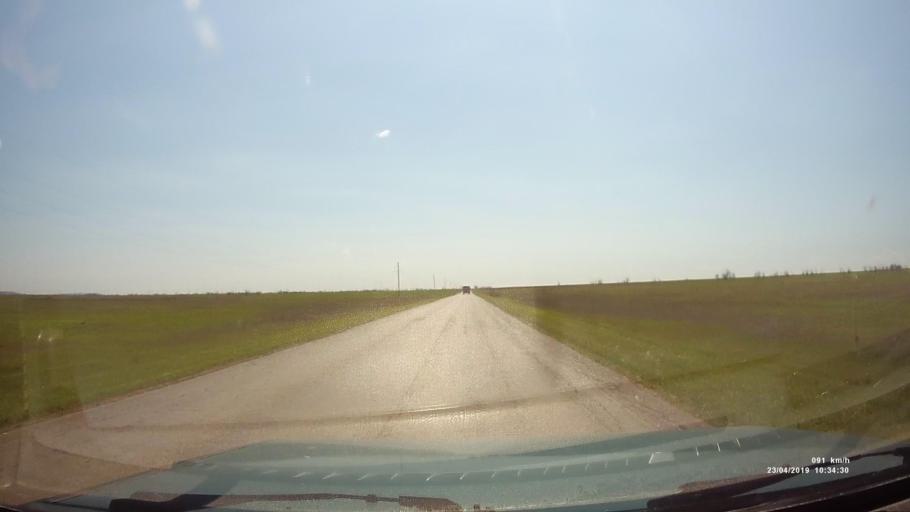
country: RU
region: Kalmykiya
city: Yashalta
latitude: 46.5634
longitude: 42.6112
